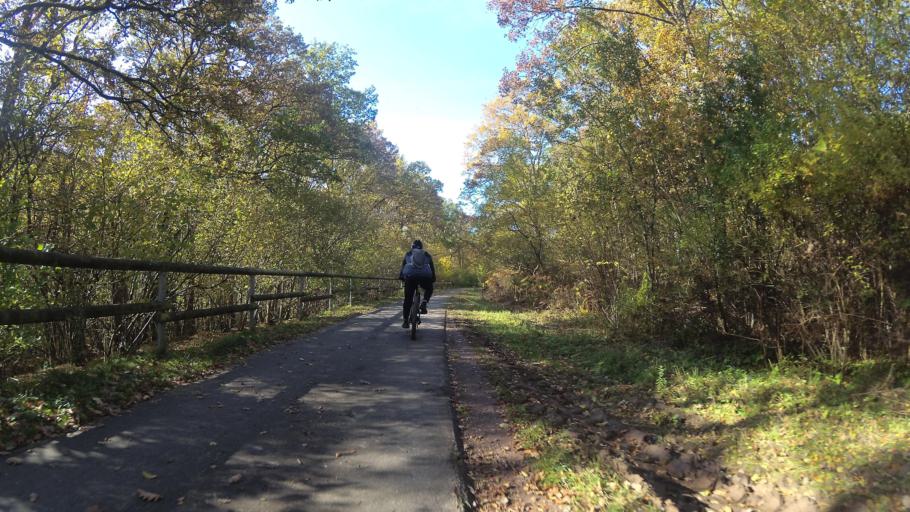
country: DE
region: Rheinland-Pfalz
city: Hentern
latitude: 49.6050
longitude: 6.7152
